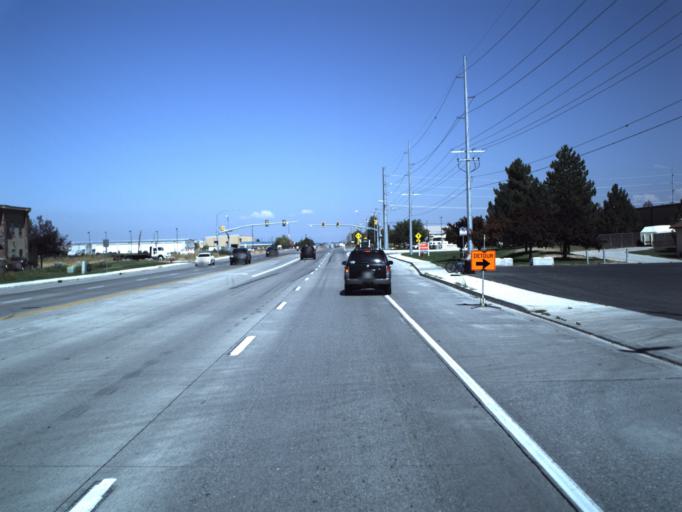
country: US
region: Utah
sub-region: Cache County
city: Logan
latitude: 41.7561
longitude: -111.8588
